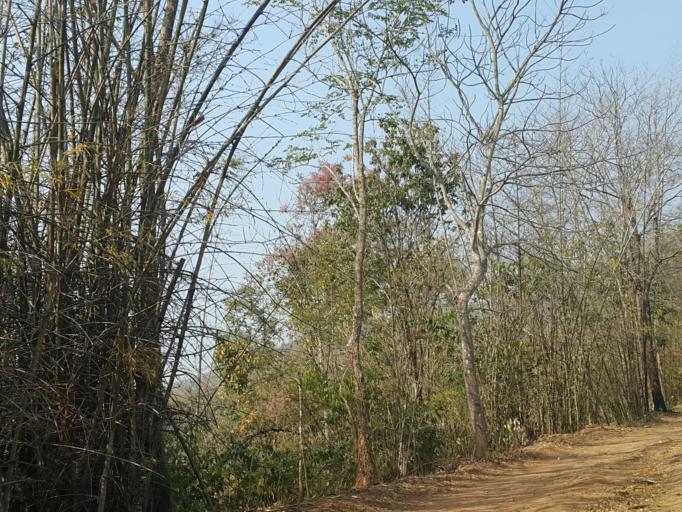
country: TH
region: Chiang Mai
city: Hang Dong
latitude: 18.7317
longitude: 98.8574
